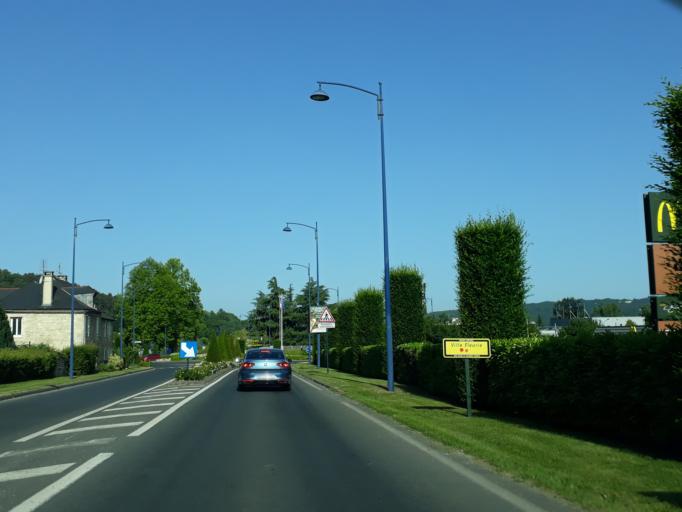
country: FR
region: Aquitaine
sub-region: Departement de la Dordogne
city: Terrasson-Lavilledieu
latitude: 45.1284
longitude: 1.3258
